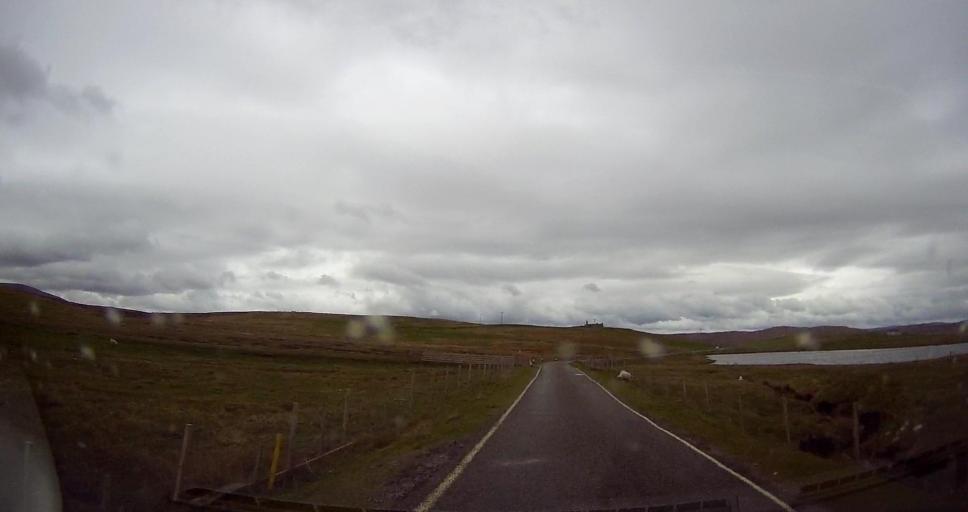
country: GB
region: Scotland
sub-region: Shetland Islands
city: Lerwick
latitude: 60.4867
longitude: -1.5133
